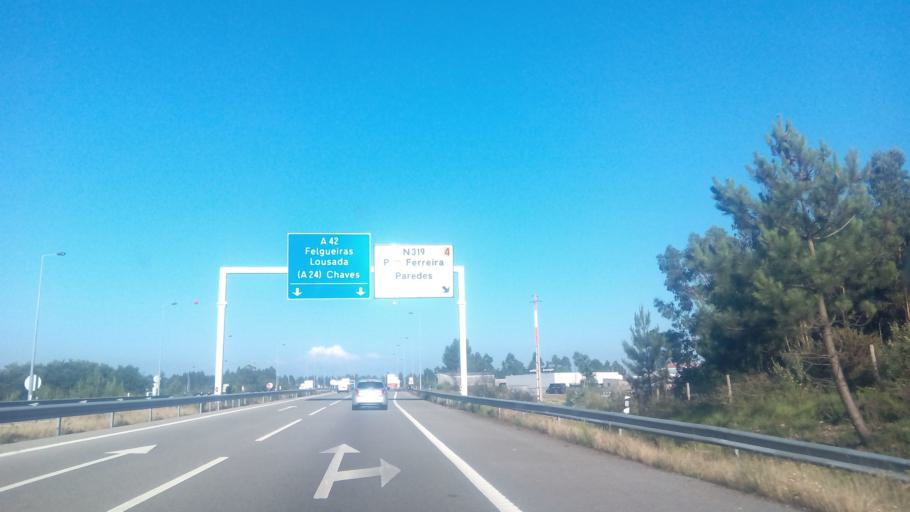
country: PT
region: Porto
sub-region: Pacos de Ferreira
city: Pacos de Ferreira
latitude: 41.2592
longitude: -8.3675
